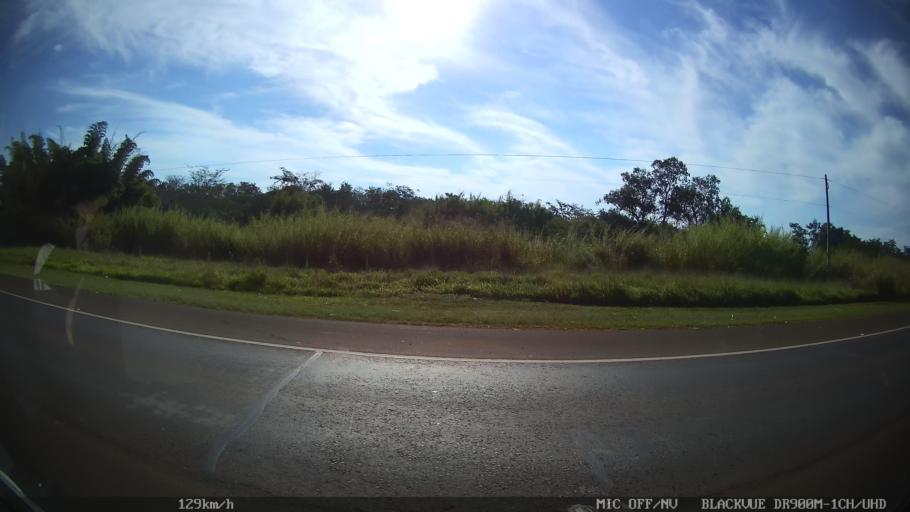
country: BR
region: Sao Paulo
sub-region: Araraquara
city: Araraquara
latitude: -21.7878
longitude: -48.1229
